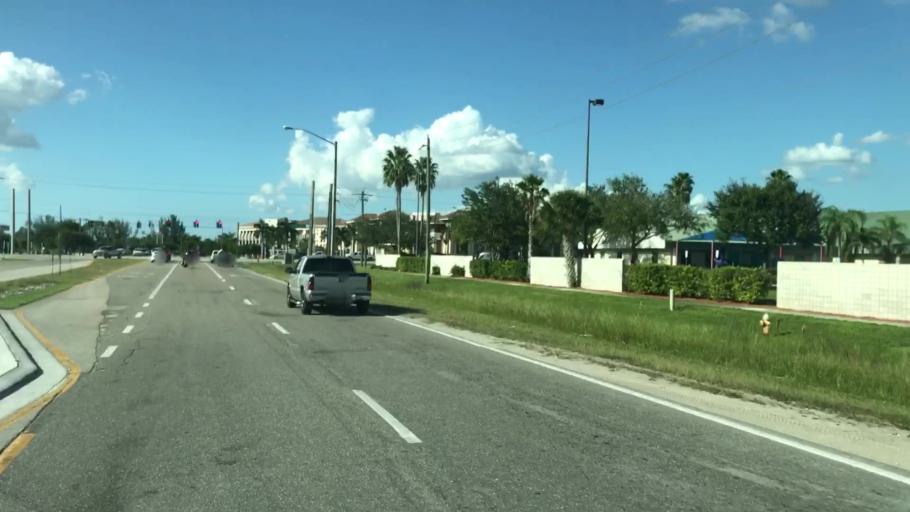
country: US
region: Florida
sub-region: Lee County
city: Fort Myers
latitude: 26.6087
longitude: -81.8201
